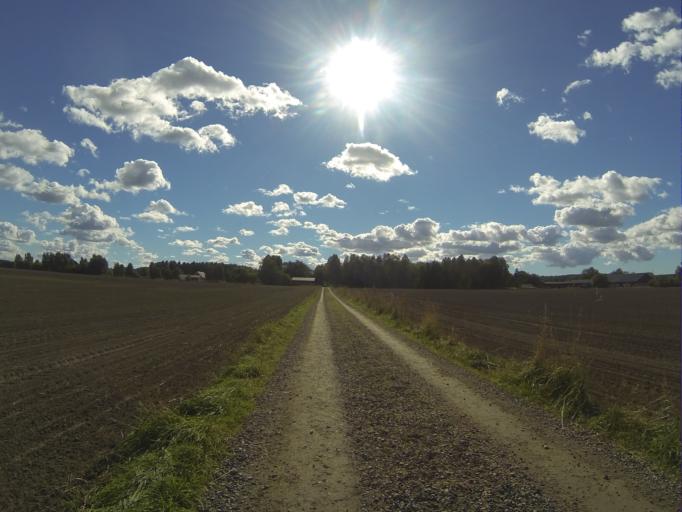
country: SE
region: Skane
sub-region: Lunds Kommun
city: Genarp
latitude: 55.7204
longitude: 13.3858
